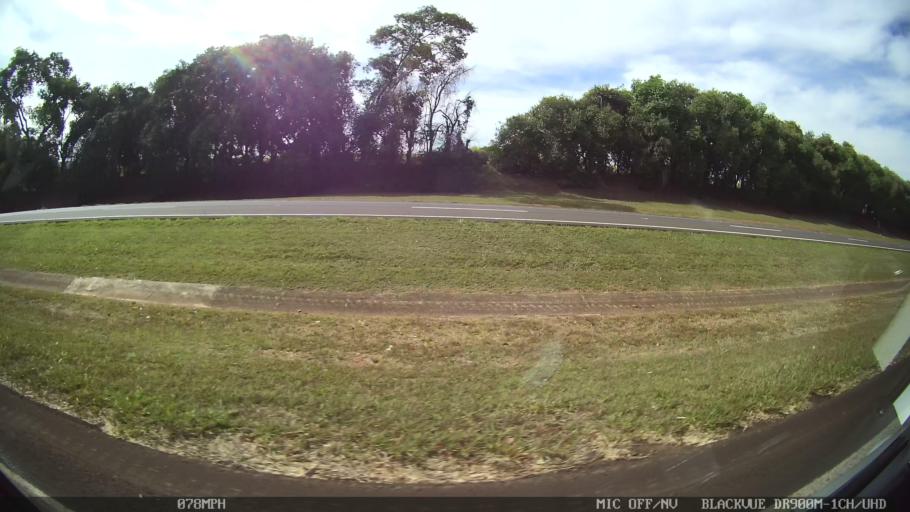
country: BR
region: Sao Paulo
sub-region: Matao
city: Matao
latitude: -21.6241
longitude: -48.4104
